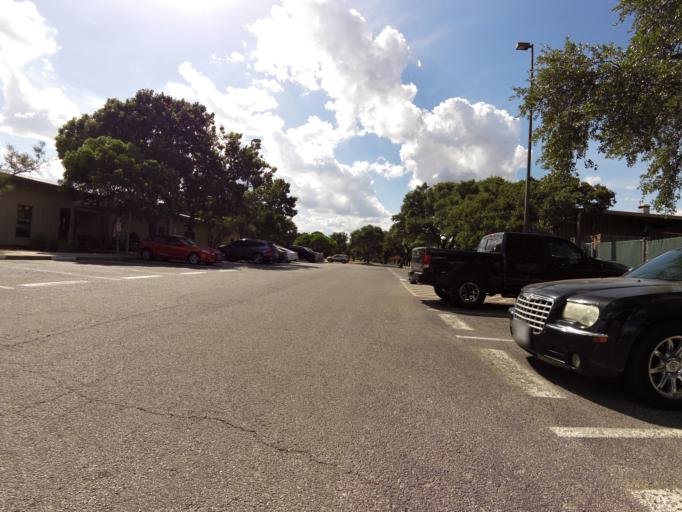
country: US
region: Texas
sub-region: Bexar County
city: Helotes
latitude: 29.5827
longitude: -98.6288
